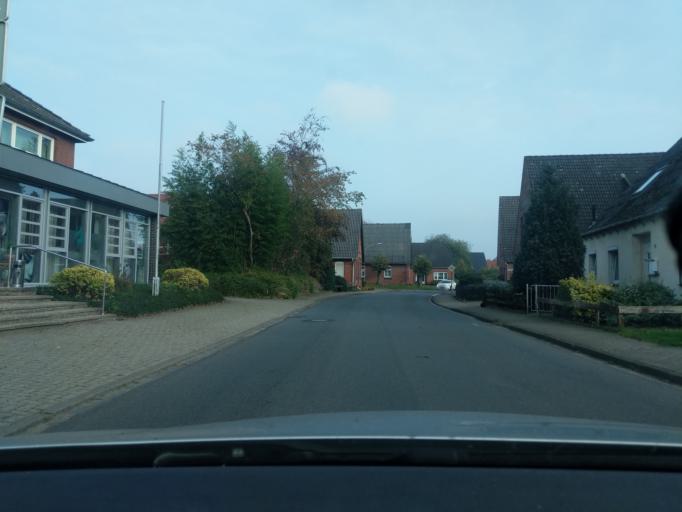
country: DE
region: Lower Saxony
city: Lamstedt
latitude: 53.6364
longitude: 9.0975
